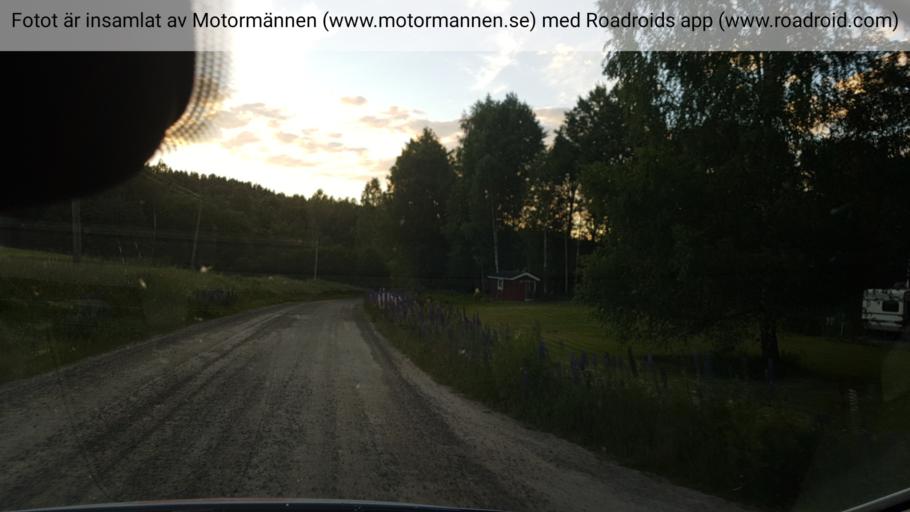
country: SE
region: Vaermland
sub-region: Sunne Kommun
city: Sunne
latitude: 59.6863
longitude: 12.8922
